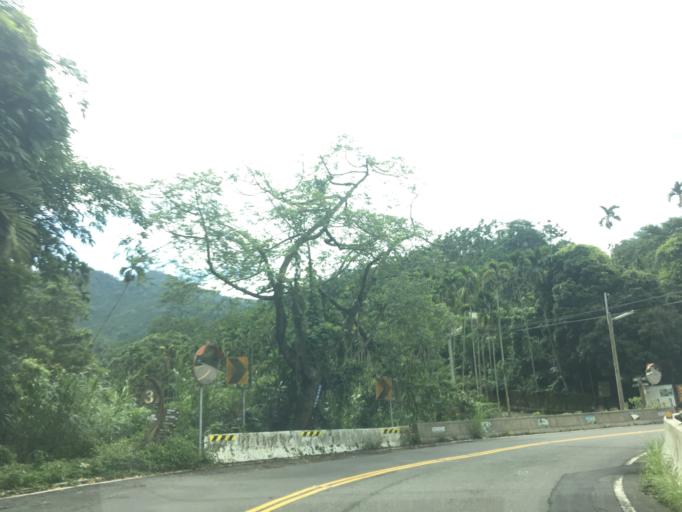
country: TW
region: Taiwan
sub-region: Yunlin
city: Douliu
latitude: 23.5643
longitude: 120.5755
